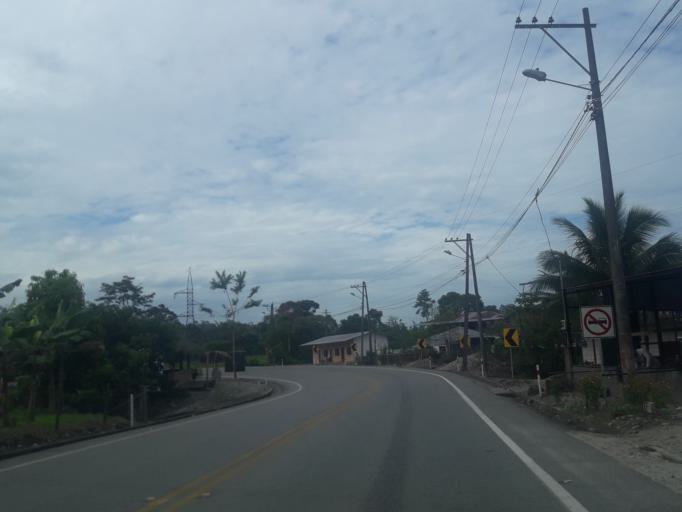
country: EC
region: Napo
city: Tena
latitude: -1.0470
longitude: -77.7964
